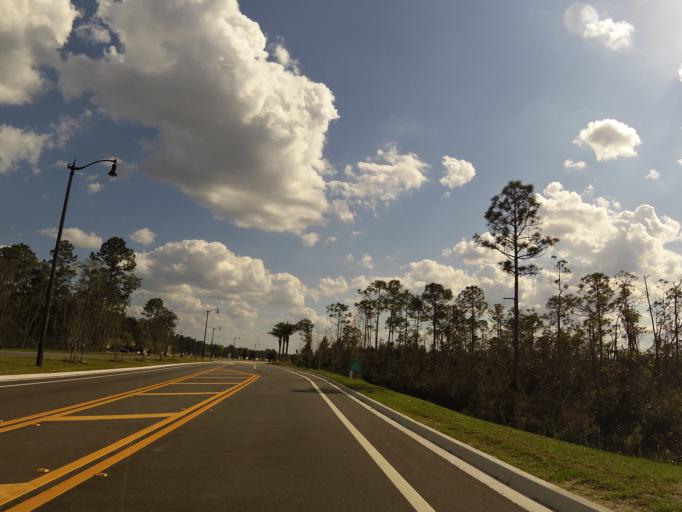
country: US
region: Florida
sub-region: Saint Johns County
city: Palm Valley
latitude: 30.1839
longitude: -81.5031
